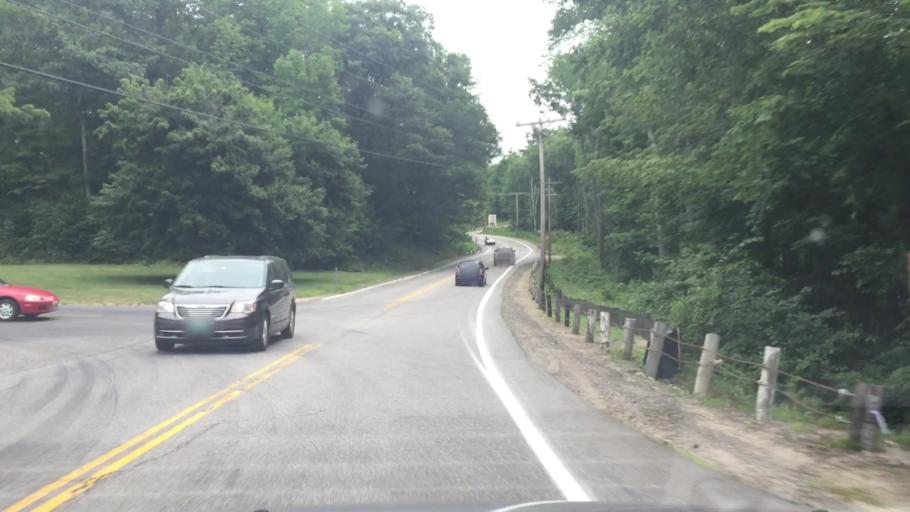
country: US
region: New Hampshire
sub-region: Carroll County
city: Moultonborough
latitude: 43.7437
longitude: -71.4099
